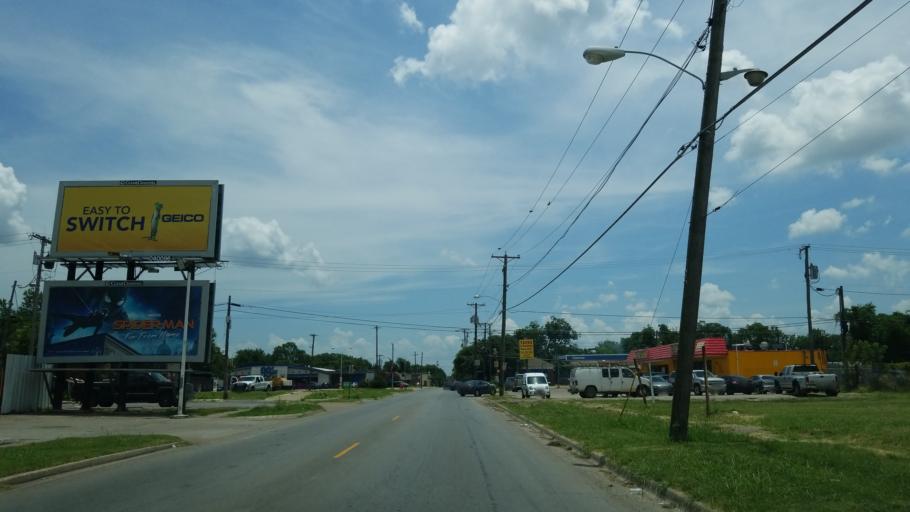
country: US
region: Texas
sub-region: Dallas County
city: Dallas
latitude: 32.8002
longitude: -96.7775
